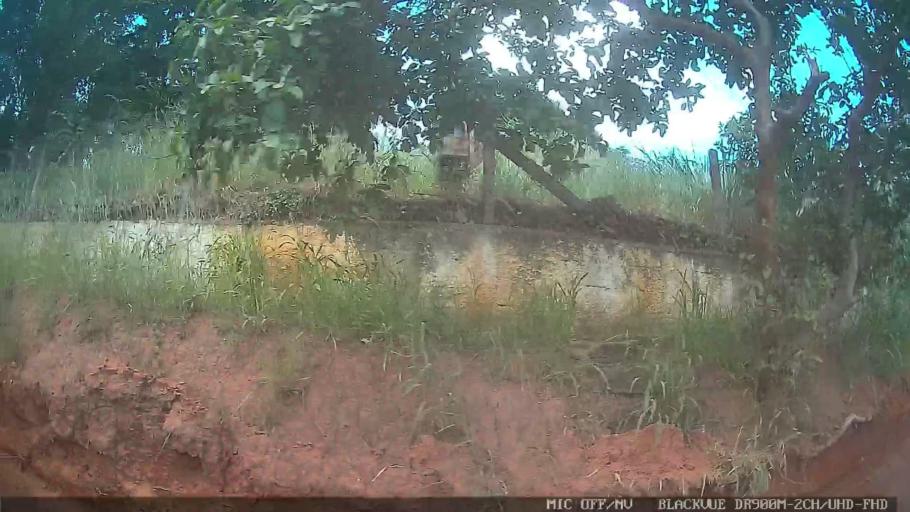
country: BR
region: Sao Paulo
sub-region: Braganca Paulista
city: Braganca Paulista
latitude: -23.0240
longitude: -46.5383
